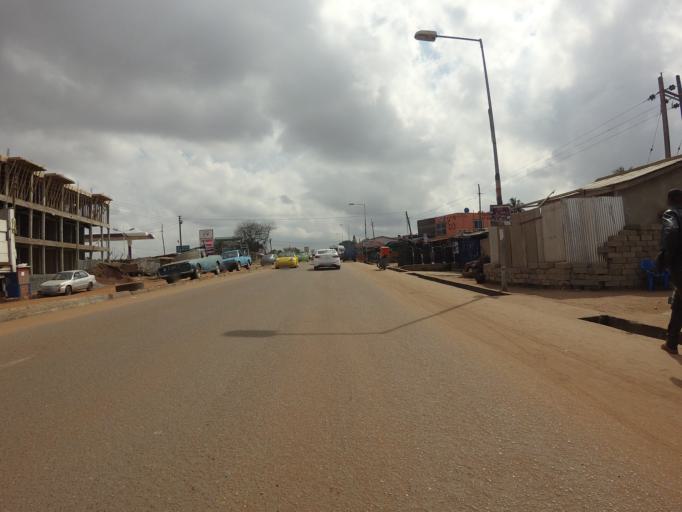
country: GH
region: Greater Accra
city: Teshi Old Town
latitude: 5.6068
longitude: -0.1141
